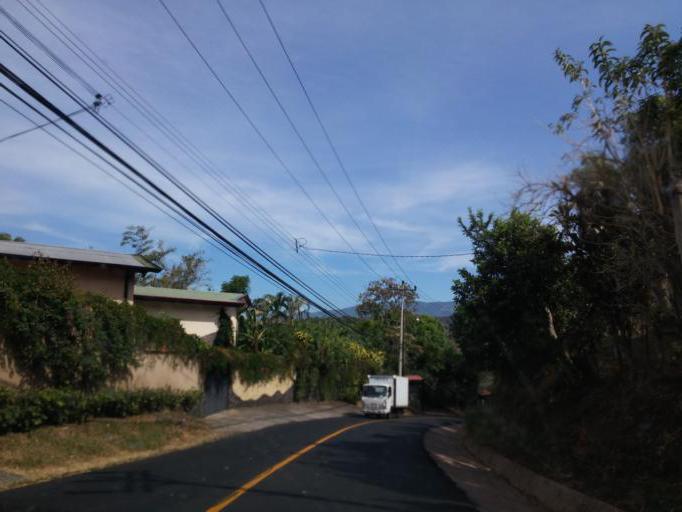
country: CR
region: Alajuela
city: Alajuela
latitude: 10.0305
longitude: -84.2255
